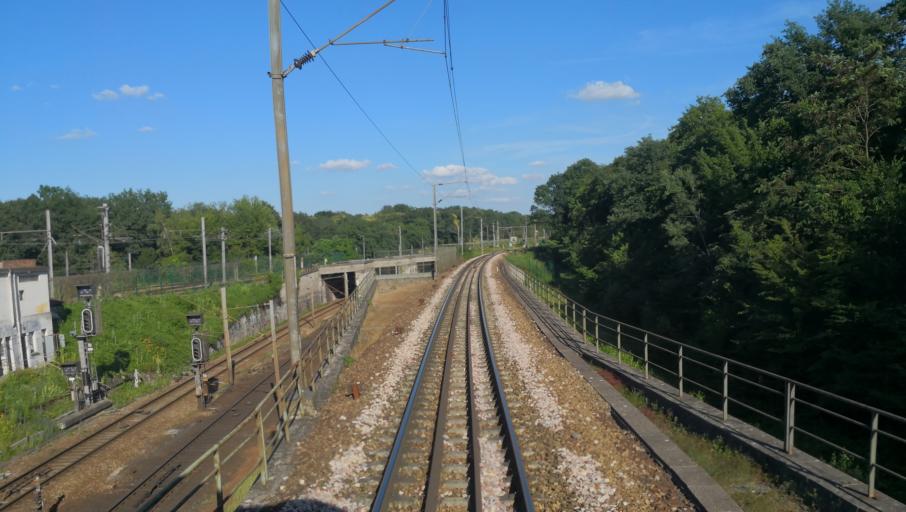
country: FR
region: Ile-de-France
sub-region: Departement des Yvelines
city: Le Mesnil-le-Roi
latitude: 48.9578
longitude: 2.1235
